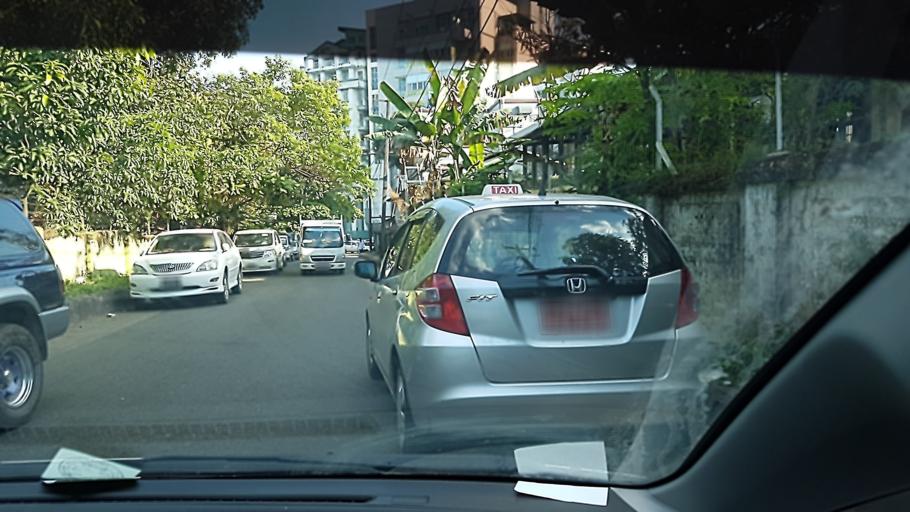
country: MM
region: Yangon
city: Yangon
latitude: 16.8119
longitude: 96.1655
